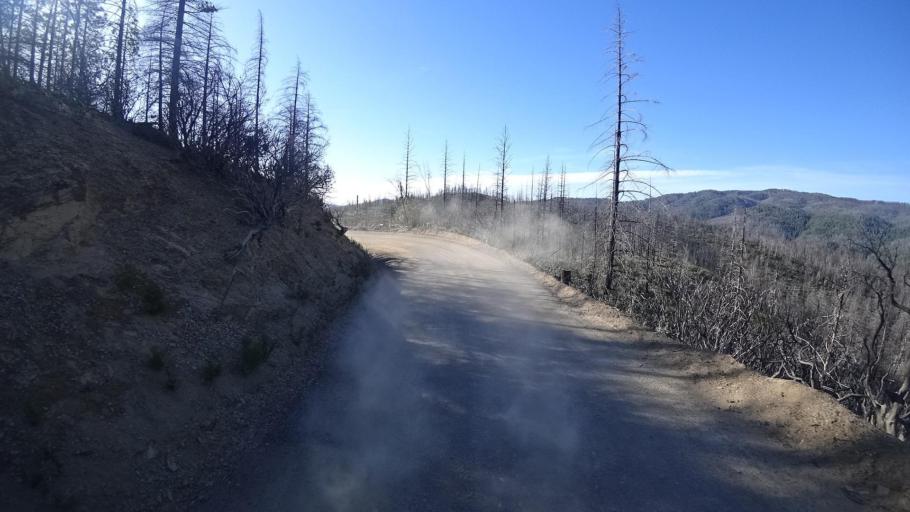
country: US
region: California
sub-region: Lake County
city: Upper Lake
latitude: 39.3452
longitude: -122.9659
